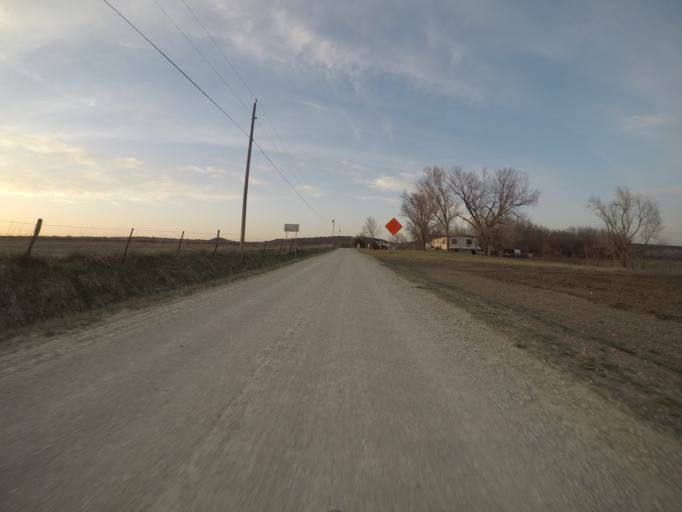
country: US
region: Kansas
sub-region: Riley County
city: Ogden
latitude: 39.1573
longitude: -96.6679
